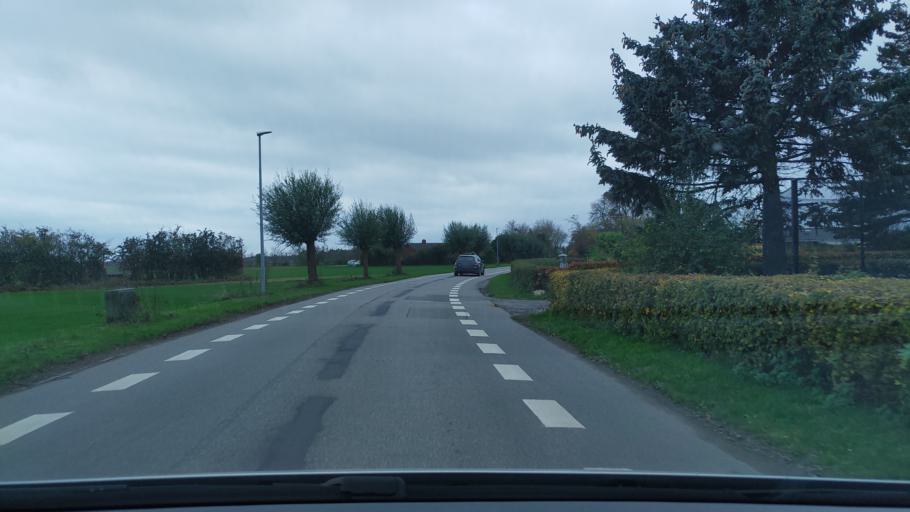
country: DK
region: Capital Region
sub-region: Tarnby Kommune
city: Tarnby
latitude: 55.5978
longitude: 12.6018
